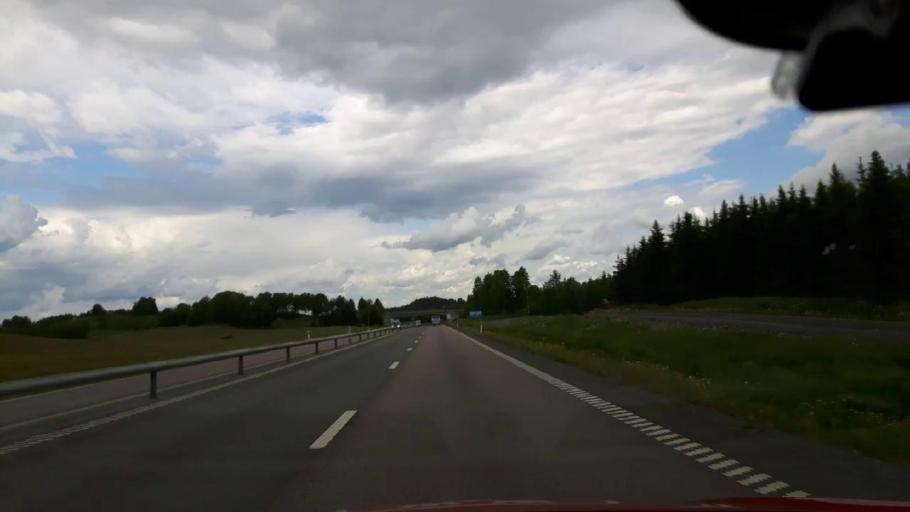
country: SE
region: Jaemtland
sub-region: Krokoms Kommun
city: Krokom
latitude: 63.3029
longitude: 14.4928
